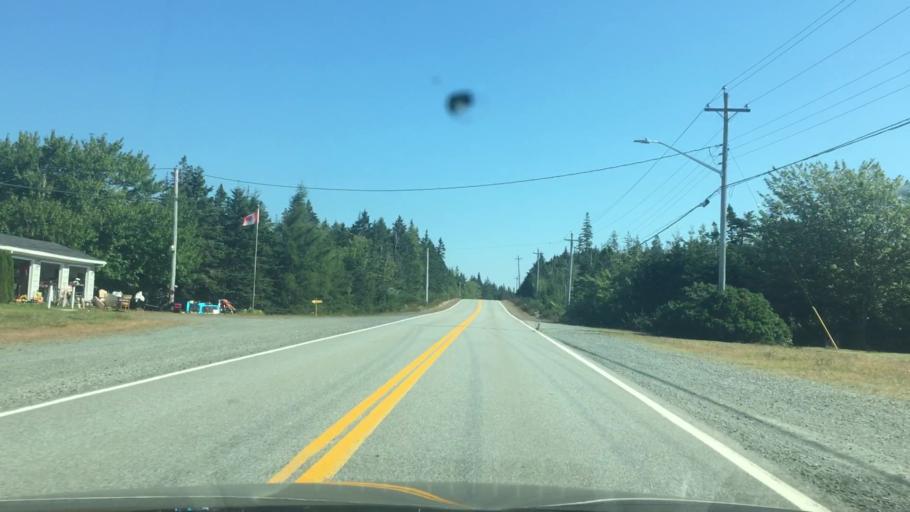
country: CA
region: Nova Scotia
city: Cole Harbour
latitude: 44.8024
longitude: -62.7121
